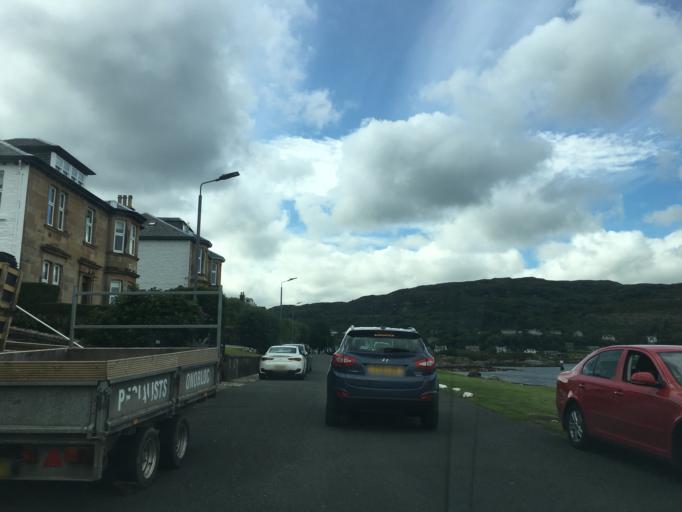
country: GB
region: Scotland
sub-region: Argyll and Bute
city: Tarbert
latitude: 55.8656
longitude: -5.4003
